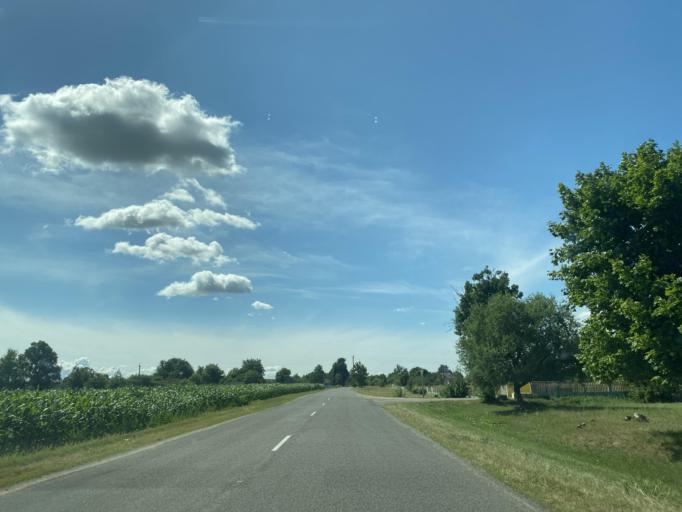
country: BY
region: Brest
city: Ivanava
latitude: 52.2100
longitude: 25.6291
